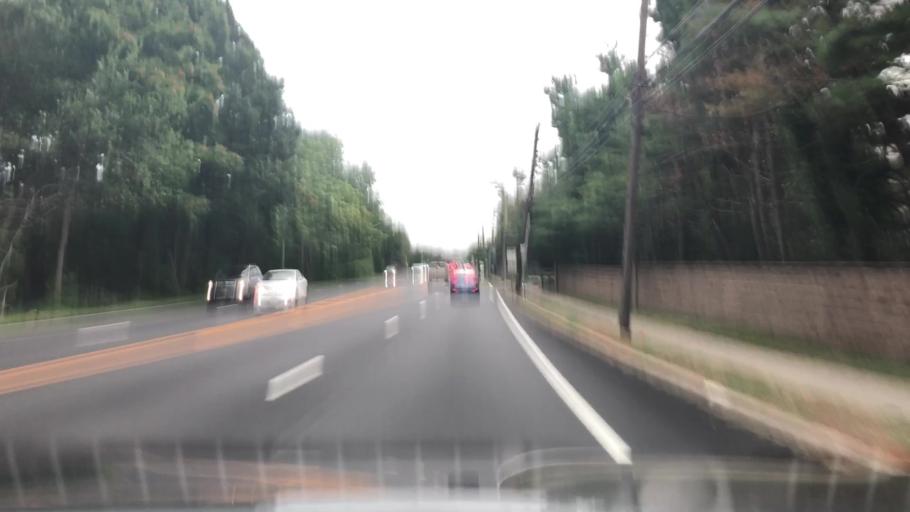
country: US
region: New York
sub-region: Nassau County
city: Woodbury
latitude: 40.8138
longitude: -73.4800
